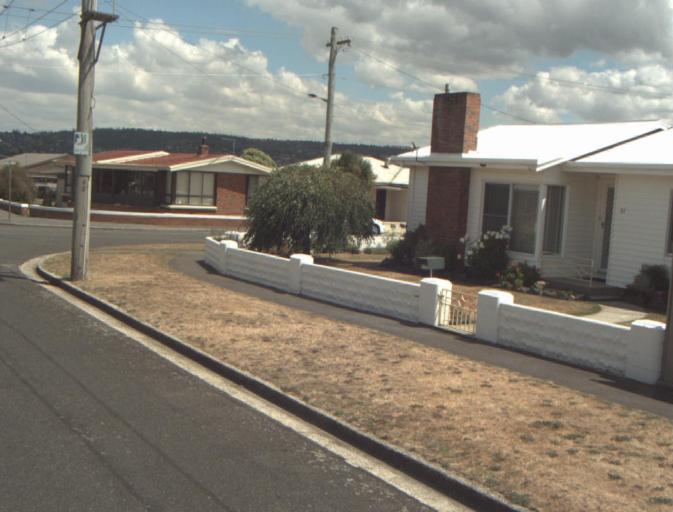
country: AU
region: Tasmania
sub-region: Launceston
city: Newnham
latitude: -41.4074
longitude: 147.1423
